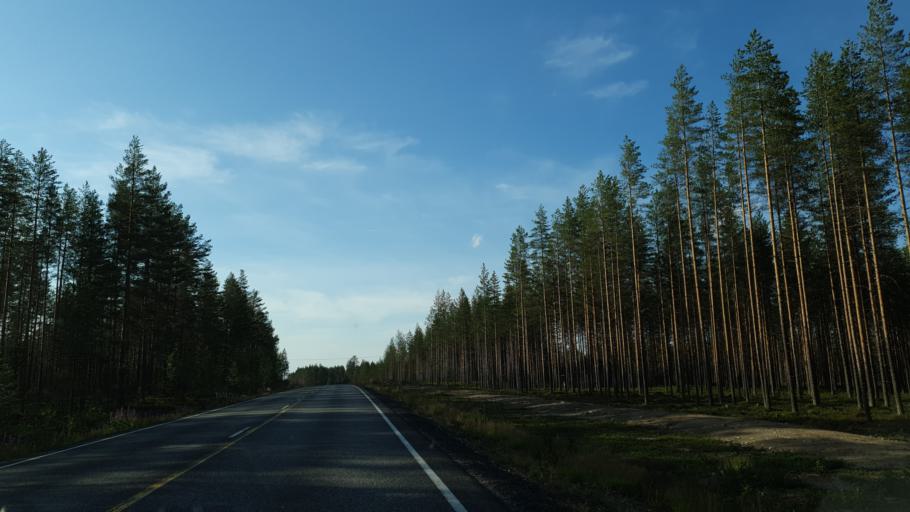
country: FI
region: Kainuu
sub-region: Kehys-Kainuu
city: Kuhmo
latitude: 64.0899
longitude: 29.4814
